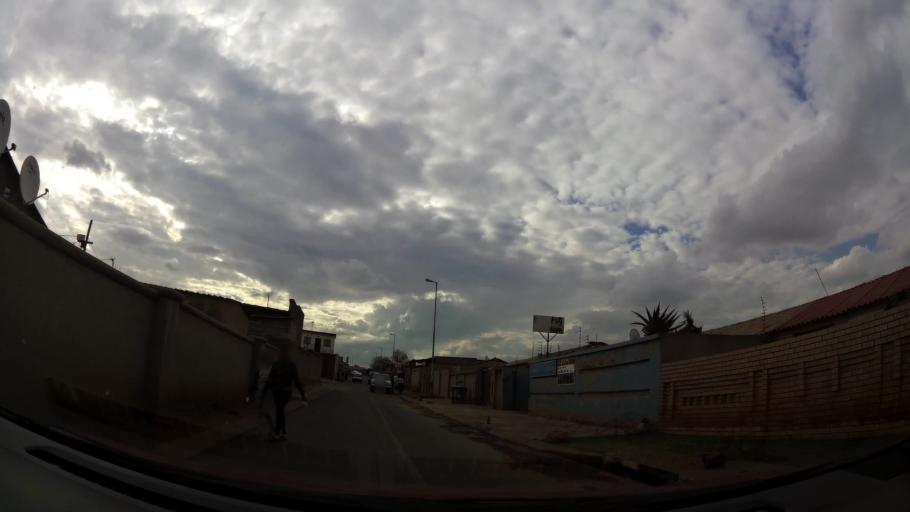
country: ZA
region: Gauteng
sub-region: City of Johannesburg Metropolitan Municipality
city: Soweto
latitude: -26.2439
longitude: 27.8394
